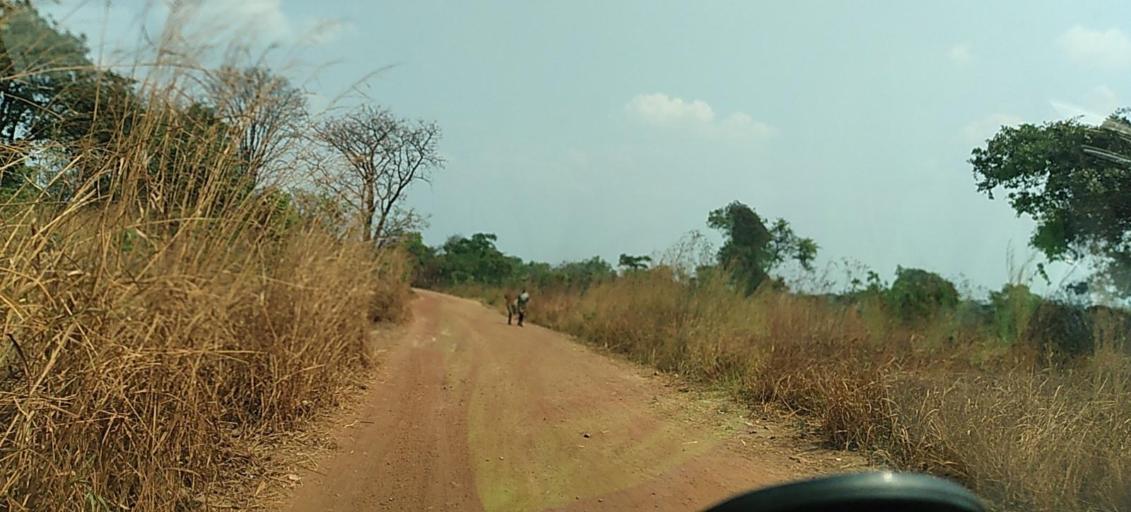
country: ZM
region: North-Western
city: Kansanshi
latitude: -12.0981
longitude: 26.3632
